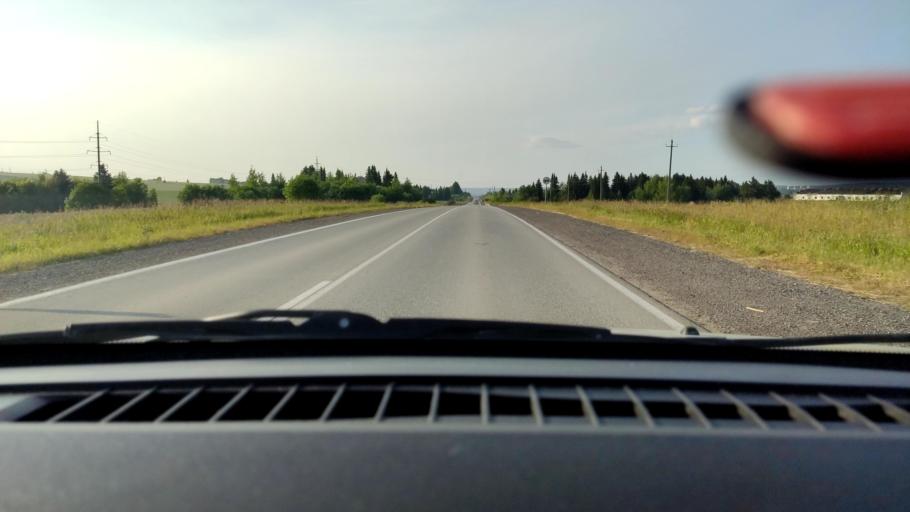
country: RU
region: Perm
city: Lobanovo
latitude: 57.8505
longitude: 56.2963
